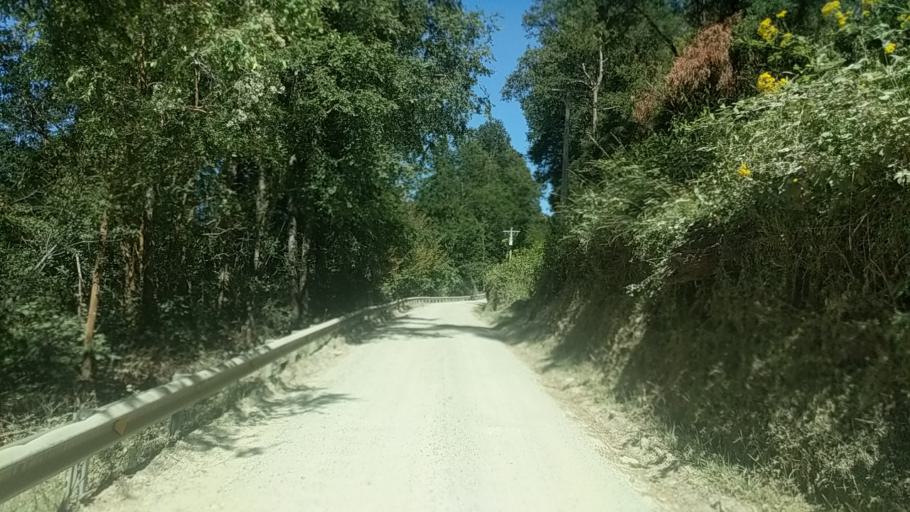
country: CL
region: Araucania
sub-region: Provincia de Cautin
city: Pucon
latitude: -39.0632
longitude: -71.7186
